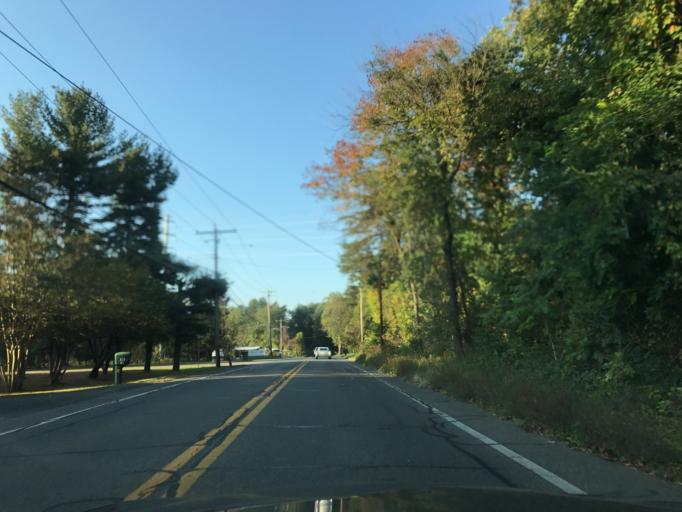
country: US
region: Maryland
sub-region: Anne Arundel County
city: Gambrills
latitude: 39.0638
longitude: -76.6300
